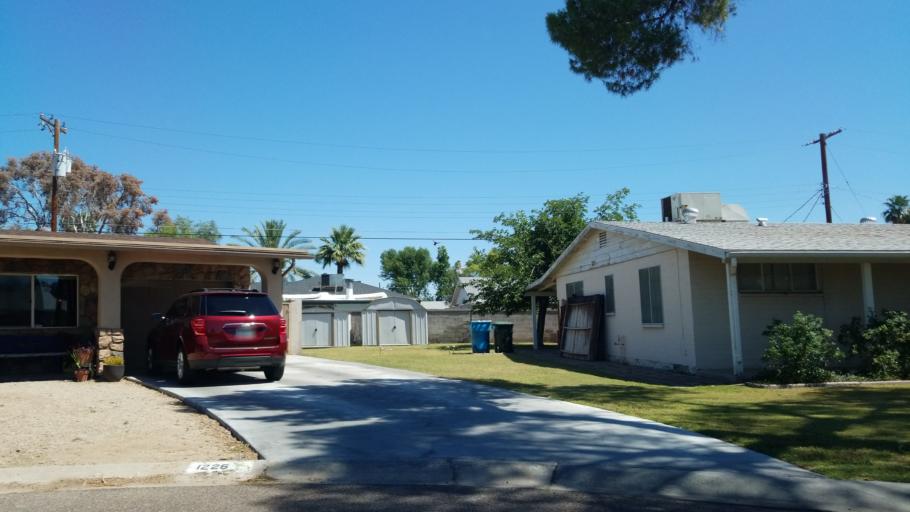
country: US
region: Arizona
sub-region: Maricopa County
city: Phoenix
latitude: 33.5038
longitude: -112.0886
